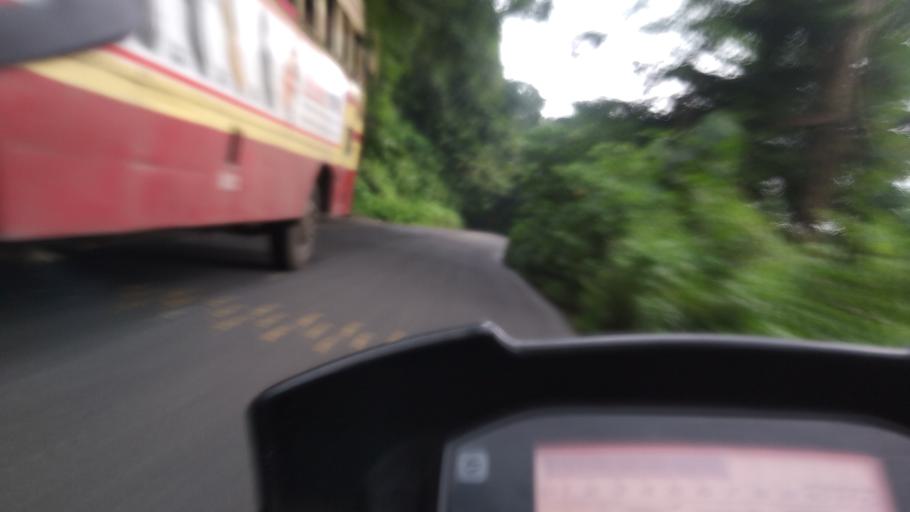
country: IN
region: Kerala
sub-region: Idukki
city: Kuttampuzha
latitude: 10.0665
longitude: 76.7822
